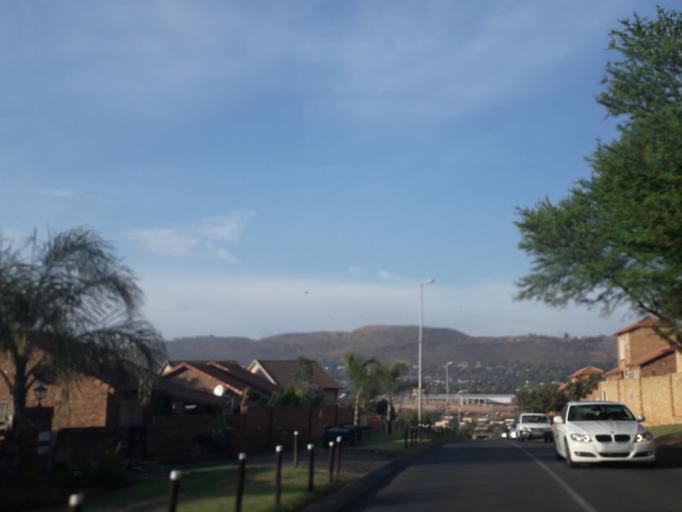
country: ZA
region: Gauteng
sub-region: City of Johannesburg Metropolitan Municipality
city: Roodepoort
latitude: -26.1051
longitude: 27.8949
